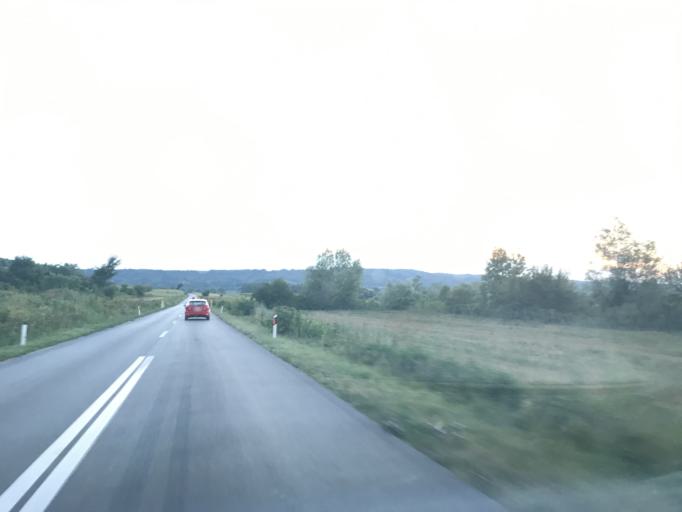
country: RS
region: Central Serbia
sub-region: Branicevski Okrug
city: Veliko Gradiste
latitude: 44.7200
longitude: 21.4151
